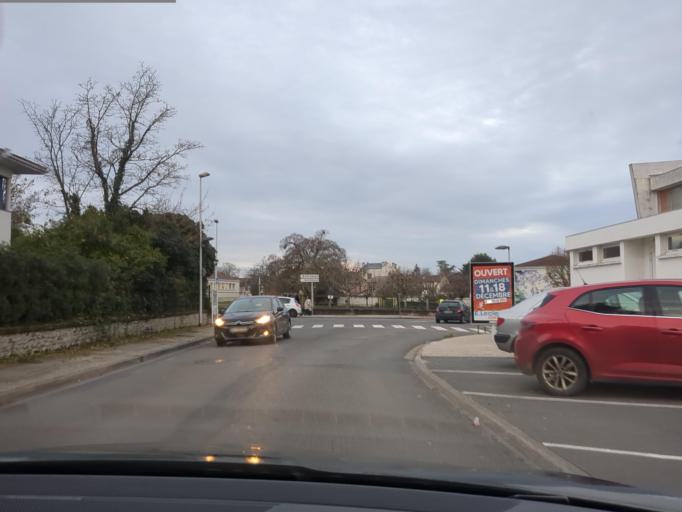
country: FR
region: Poitou-Charentes
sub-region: Departement de la Charente-Maritime
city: Jonzac
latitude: 45.4402
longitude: -0.4354
